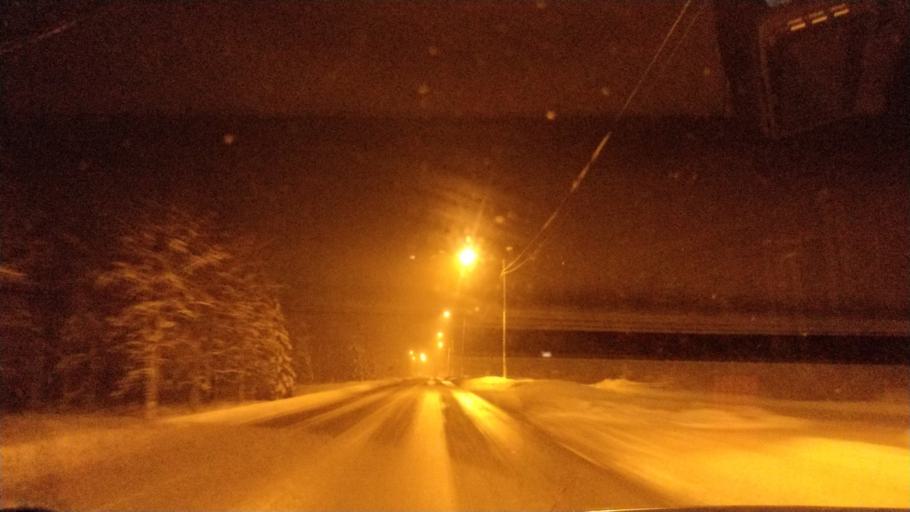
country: FI
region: Lapland
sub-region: Rovaniemi
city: Rovaniemi
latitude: 66.2789
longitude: 25.3340
